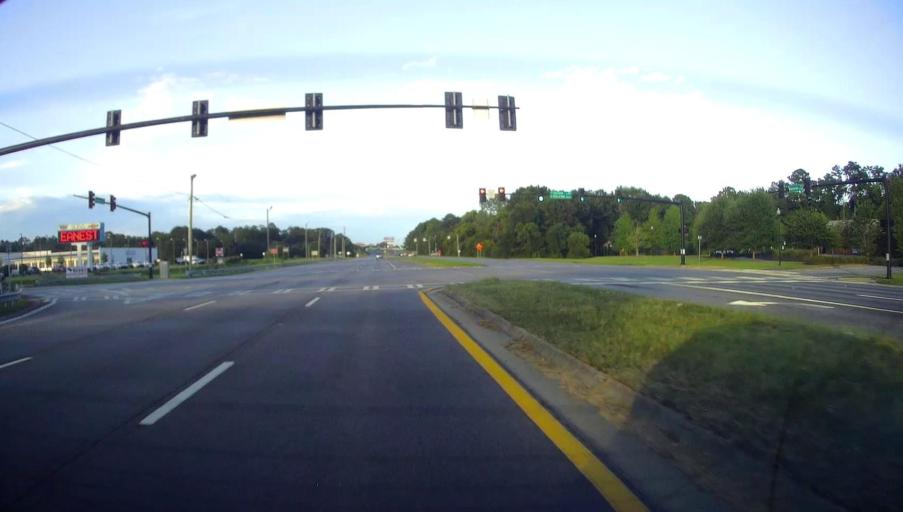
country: US
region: Georgia
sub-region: Muscogee County
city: Columbus
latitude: 32.5085
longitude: -84.9366
